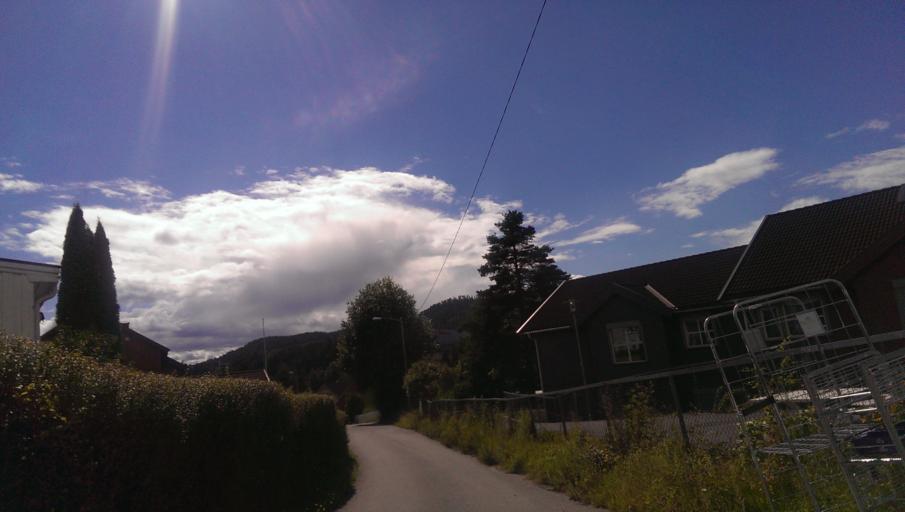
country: NO
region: Buskerud
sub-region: Kongsberg
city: Kongsberg
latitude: 59.6578
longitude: 9.6548
